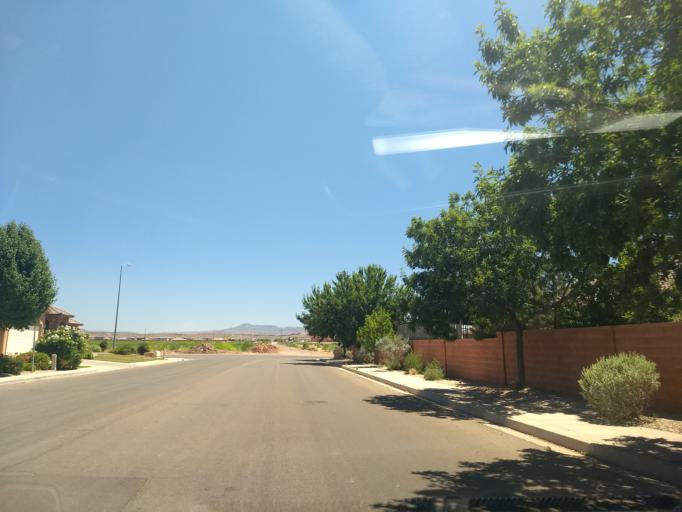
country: US
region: Utah
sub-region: Washington County
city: Washington
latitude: 37.0967
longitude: -113.5136
